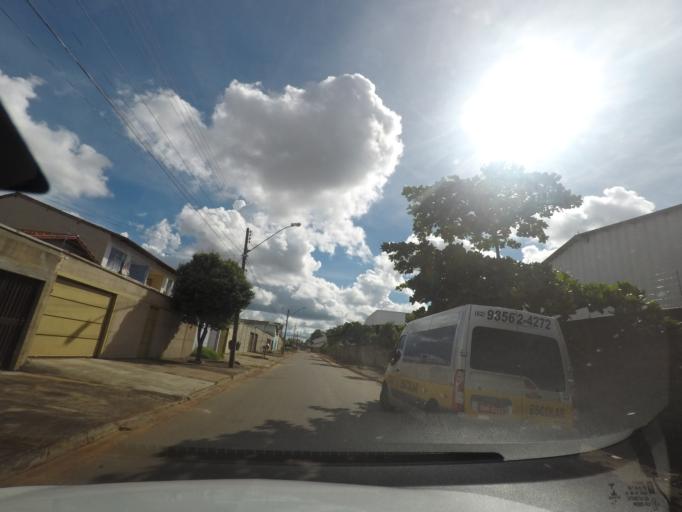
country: BR
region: Goias
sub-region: Goiania
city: Goiania
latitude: -16.7180
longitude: -49.3615
